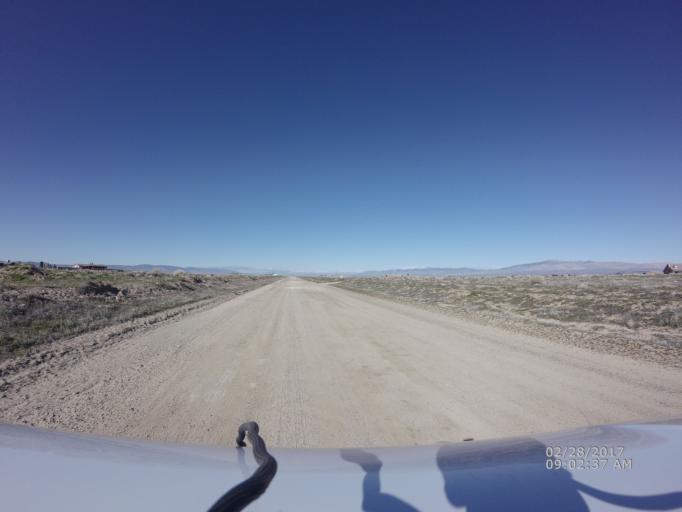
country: US
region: California
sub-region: Kern County
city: Rosamond
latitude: 34.8056
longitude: -118.2591
